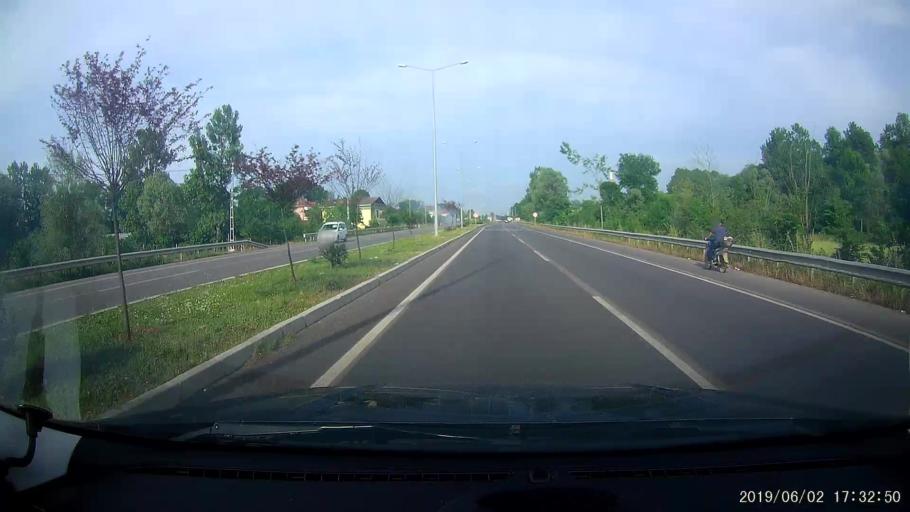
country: TR
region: Samsun
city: Carsamba
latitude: 41.2205
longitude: 36.8357
